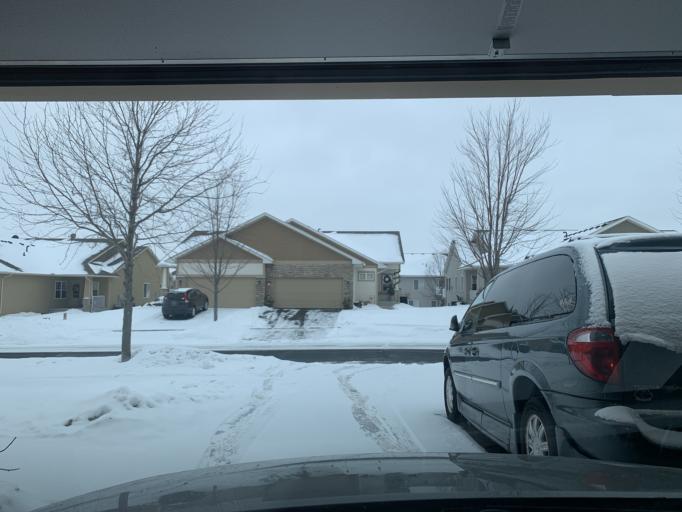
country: US
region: Minnesota
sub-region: Carver County
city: Victoria
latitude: 44.8402
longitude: -93.6546
